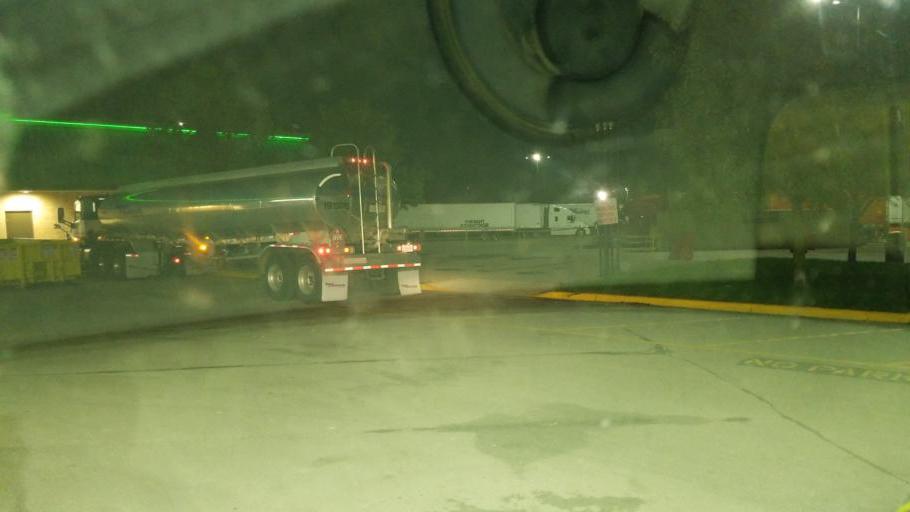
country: US
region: Ohio
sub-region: Preble County
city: New Paris
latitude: 39.8347
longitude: -84.8104
